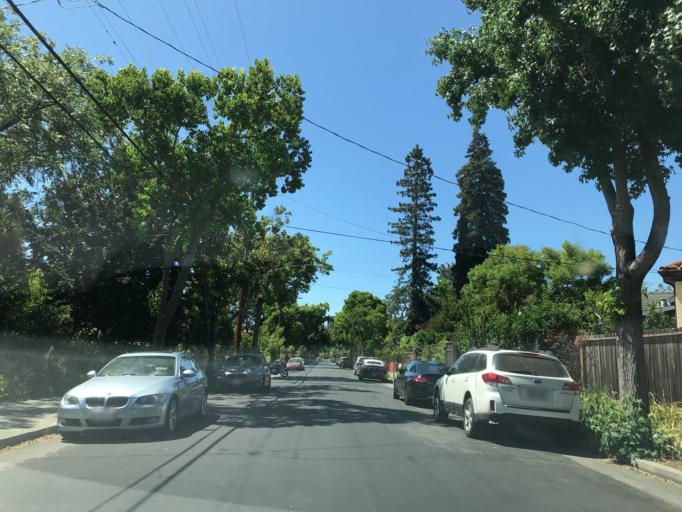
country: US
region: California
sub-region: Santa Clara County
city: Palo Alto
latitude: 37.4526
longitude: -122.1508
